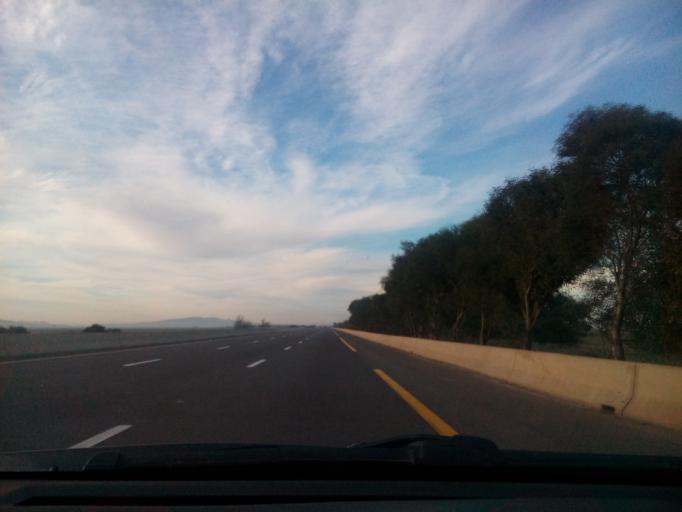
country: DZ
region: Mostaganem
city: Mostaganem
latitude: 35.6916
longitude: 0.1702
